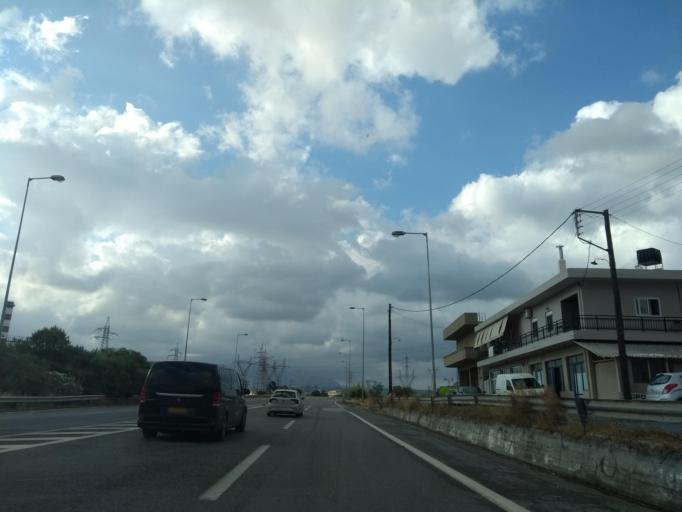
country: GR
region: Crete
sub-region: Nomos Irakleiou
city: Gazi
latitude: 35.3401
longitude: 25.0468
